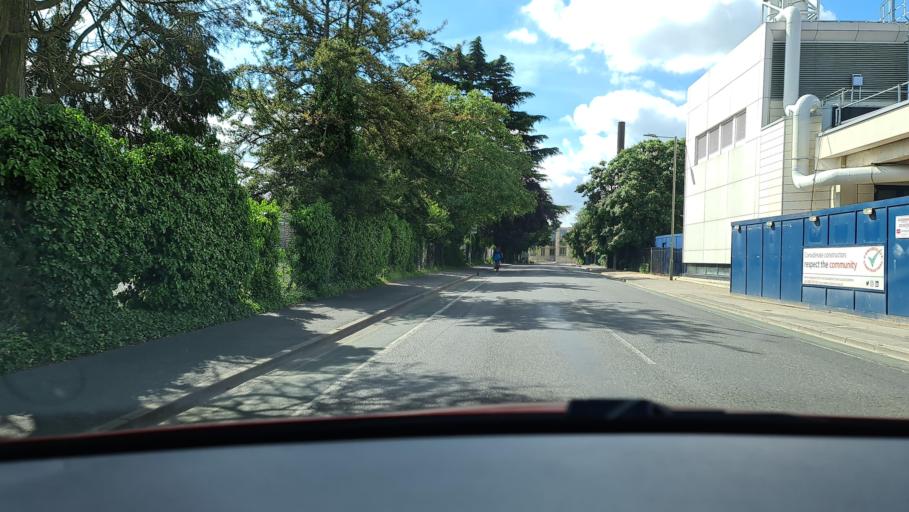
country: GB
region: England
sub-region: Oxfordshire
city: Oxford
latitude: 51.7587
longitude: -1.2500
